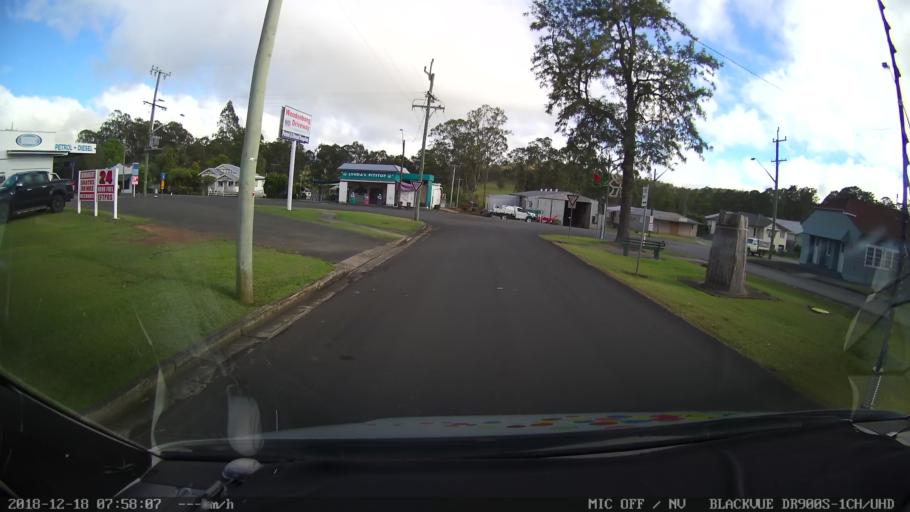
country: AU
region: New South Wales
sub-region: Kyogle
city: Kyogle
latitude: -28.3896
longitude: 152.6122
